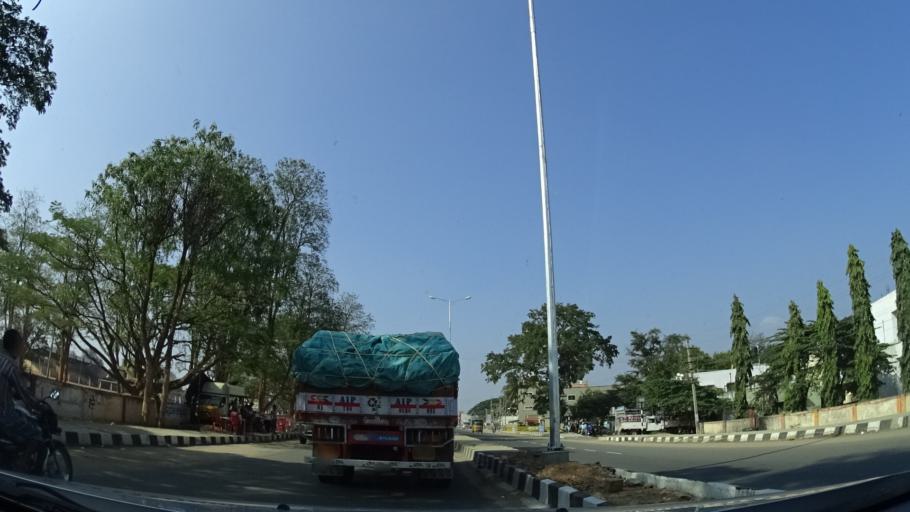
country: IN
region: Karnataka
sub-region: Chamrajnagar
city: Gundlupet
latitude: 11.8124
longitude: 76.6868
